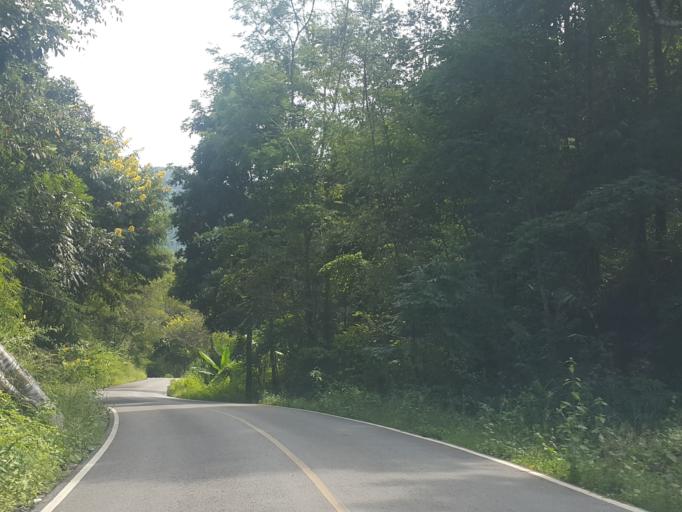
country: TH
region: Chiang Mai
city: Mae On
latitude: 18.8640
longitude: 99.2892
